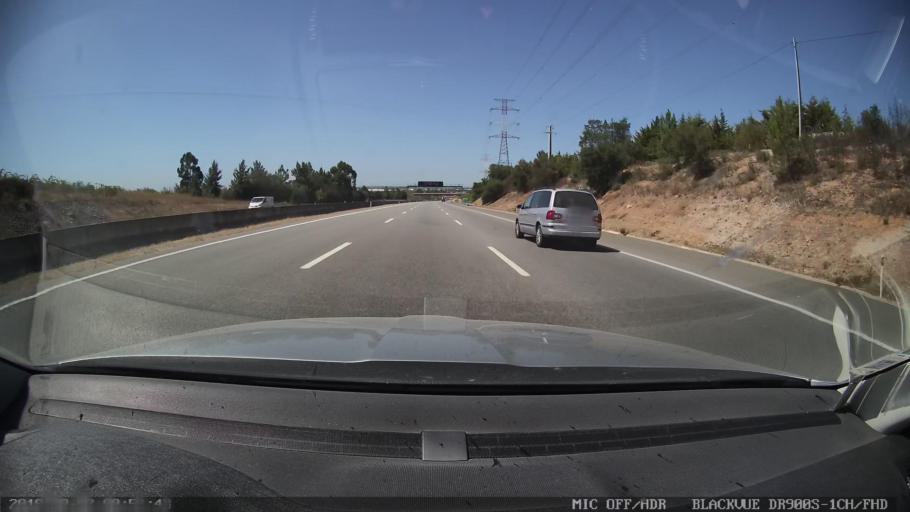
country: PT
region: Setubal
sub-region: Palmela
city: Quinta do Anjo
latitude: 38.5831
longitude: -8.9680
